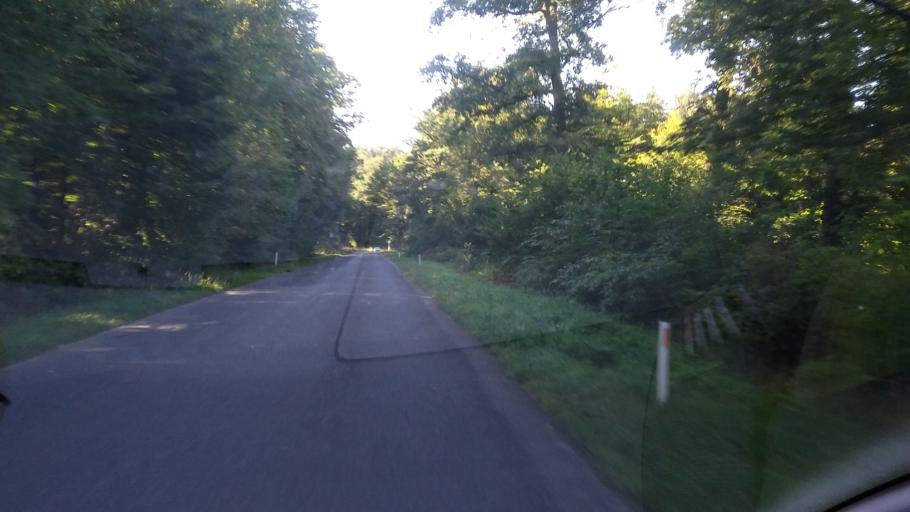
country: BE
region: Wallonia
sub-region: Province du Luxembourg
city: Neufchateau
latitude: 49.7941
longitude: 5.4165
